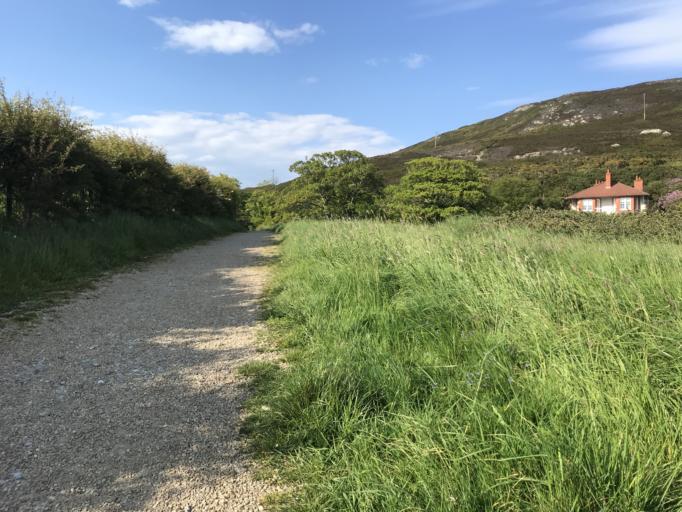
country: IE
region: Leinster
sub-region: Fingal County
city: Howth
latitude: 53.3700
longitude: -6.0869
